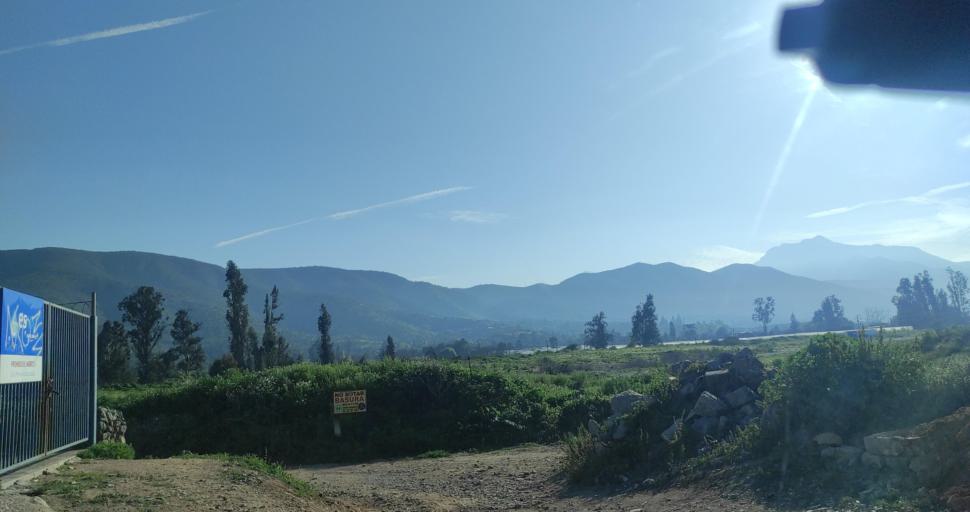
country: CL
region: Valparaiso
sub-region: Provincia de Marga Marga
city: Limache
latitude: -33.0009
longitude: -71.2529
